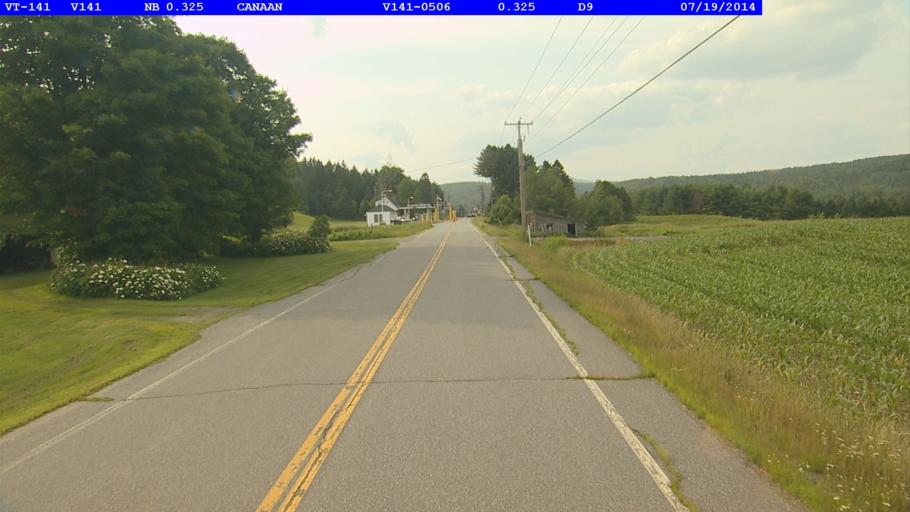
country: US
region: New Hampshire
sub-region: Coos County
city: Colebrook
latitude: 45.0107
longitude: -71.5586
